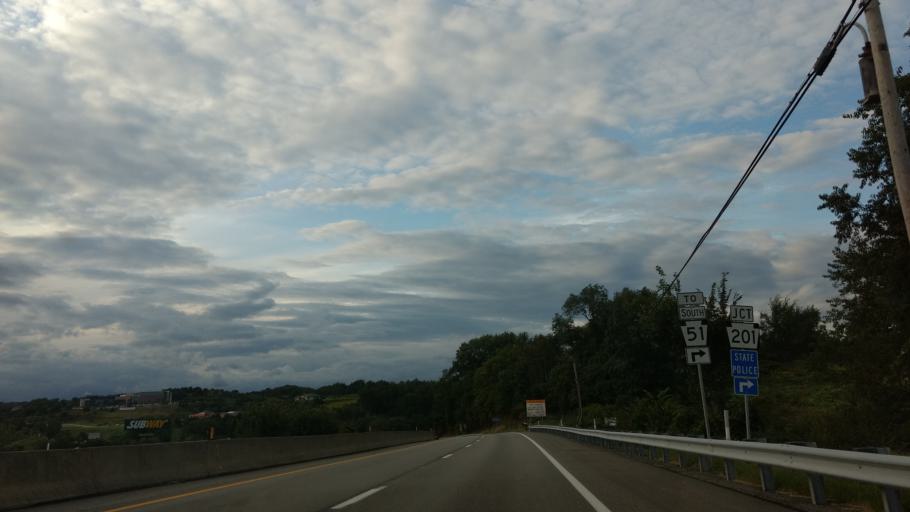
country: US
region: Pennsylvania
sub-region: Westmoreland County
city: Fellsburg
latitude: 40.1791
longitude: -79.8041
